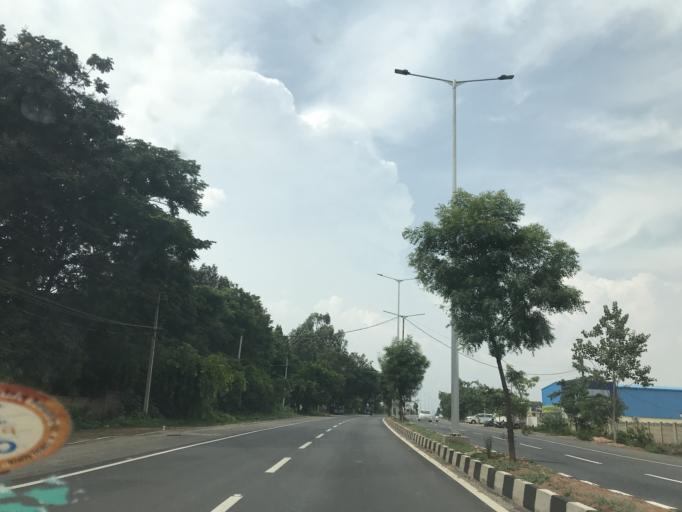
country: IN
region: Karnataka
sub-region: Bangalore Urban
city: Yelahanka
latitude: 13.1470
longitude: 77.6738
